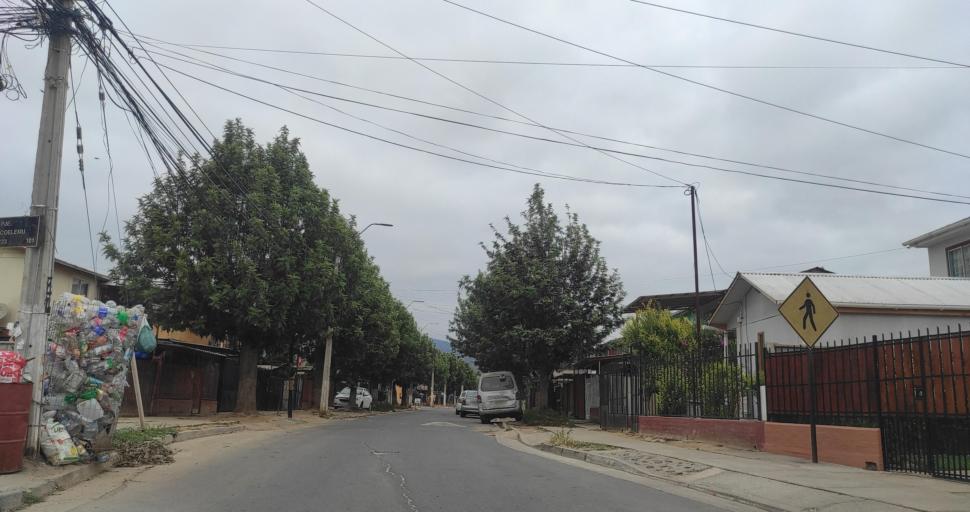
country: CL
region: Valparaiso
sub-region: Provincia de Marga Marga
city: Limache
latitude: -33.0181
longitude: -71.2637
